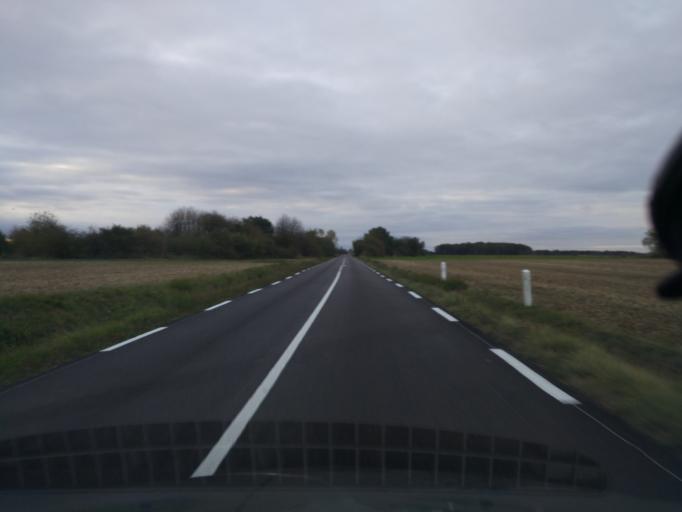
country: FR
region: Ile-de-France
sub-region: Departement de l'Essonne
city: Les Molieres
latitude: 48.6667
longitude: 2.0651
